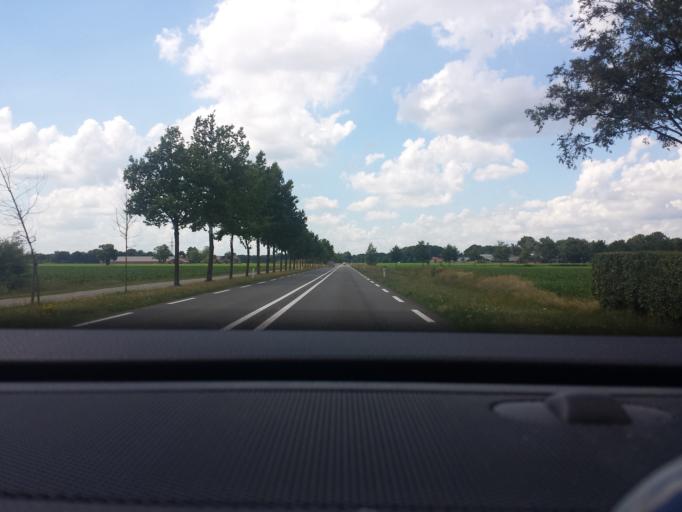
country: NL
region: Overijssel
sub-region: Gemeente Hof van Twente
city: Hengevelde
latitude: 52.1857
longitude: 6.6718
